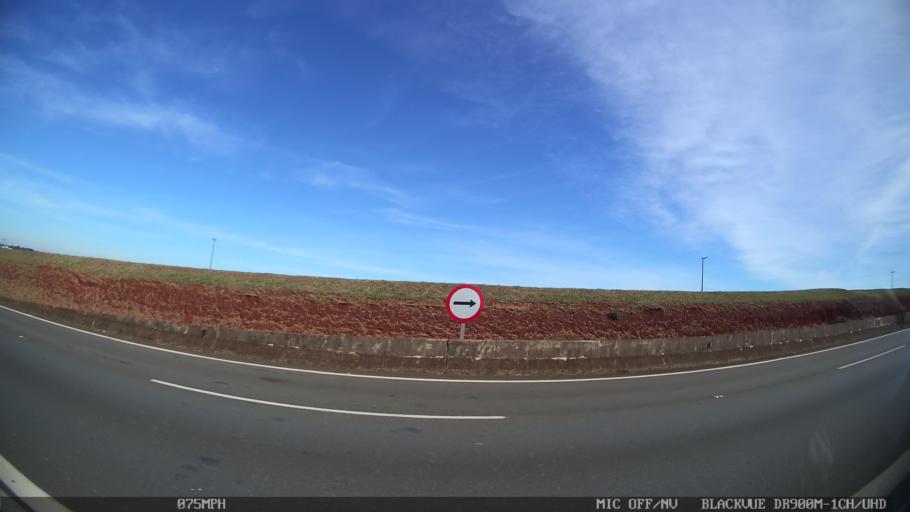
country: BR
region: Sao Paulo
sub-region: Cordeiropolis
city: Cordeiropolis
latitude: -22.4759
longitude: -47.3990
